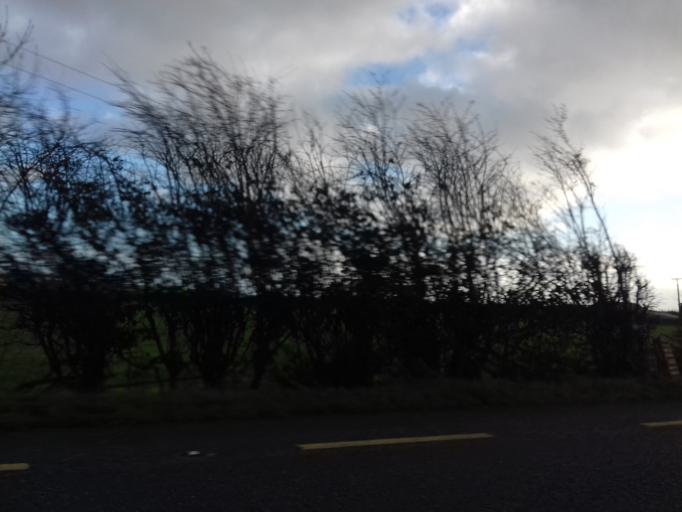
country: IE
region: Leinster
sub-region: An Mhi
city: Slane
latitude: 53.7461
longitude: -6.5050
